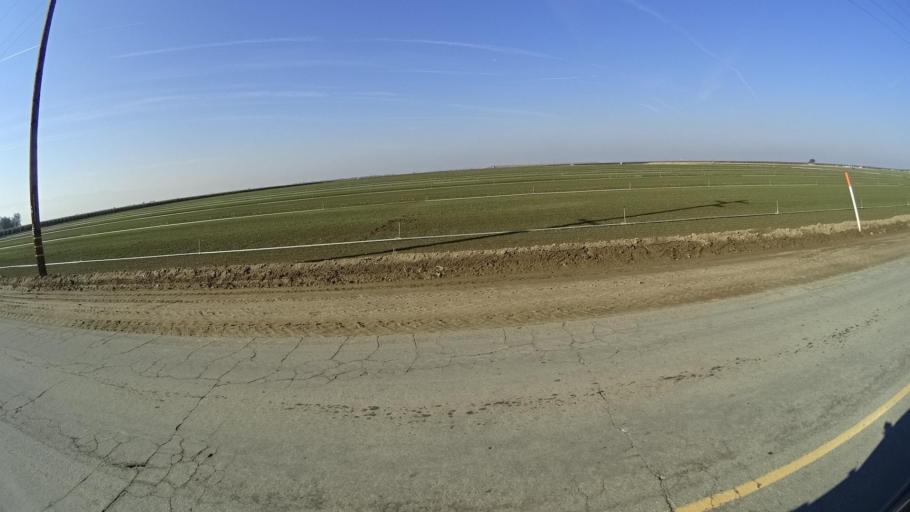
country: US
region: California
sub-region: Kern County
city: Arvin
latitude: 35.1852
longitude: -118.8781
